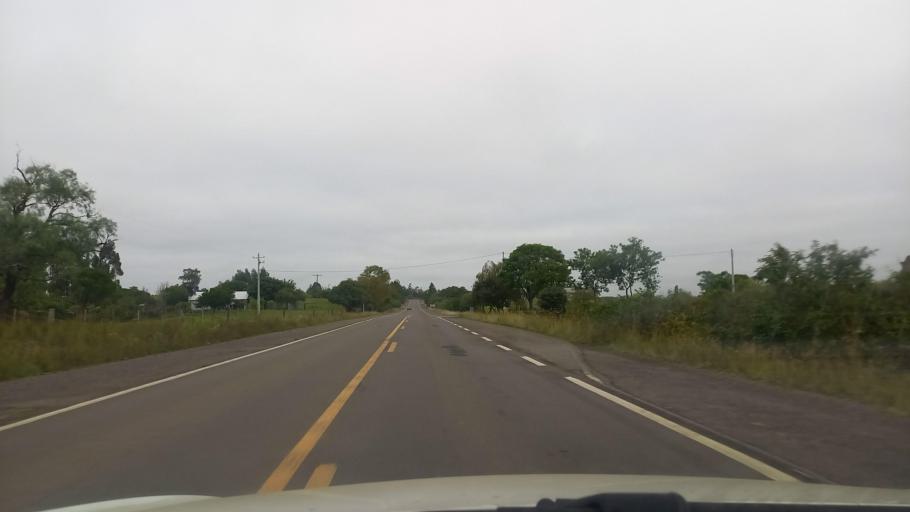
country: BR
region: Rio Grande do Sul
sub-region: Sao Pedro Do Sul
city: Sao Pedro do Sul
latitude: -29.8012
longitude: -54.1225
